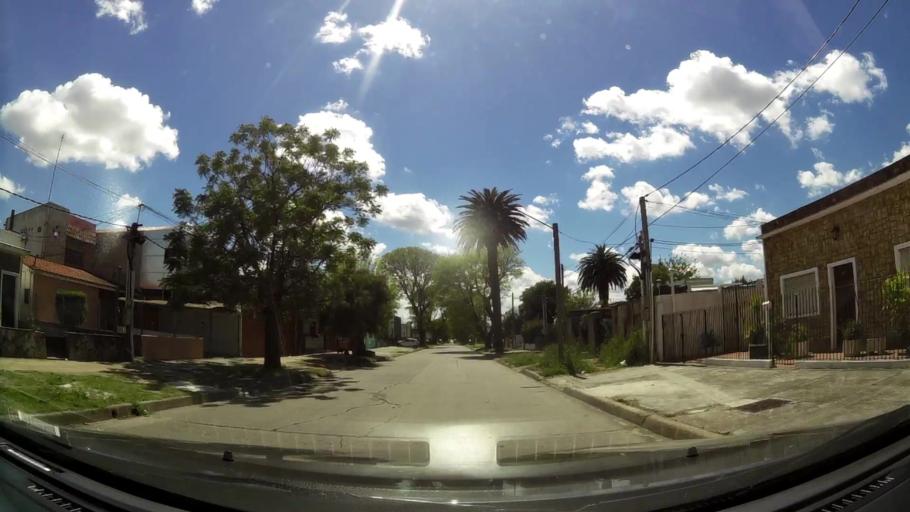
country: UY
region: Montevideo
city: Montevideo
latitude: -34.8470
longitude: -56.1335
